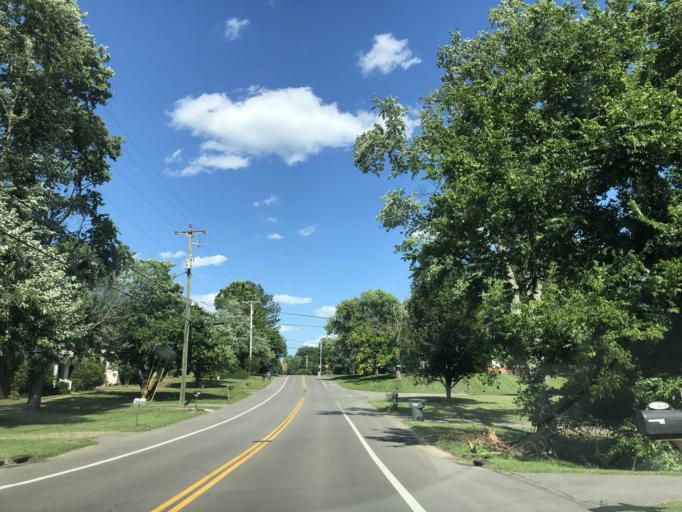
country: US
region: Tennessee
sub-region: Davidson County
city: Belle Meade
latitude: 36.0608
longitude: -86.9286
